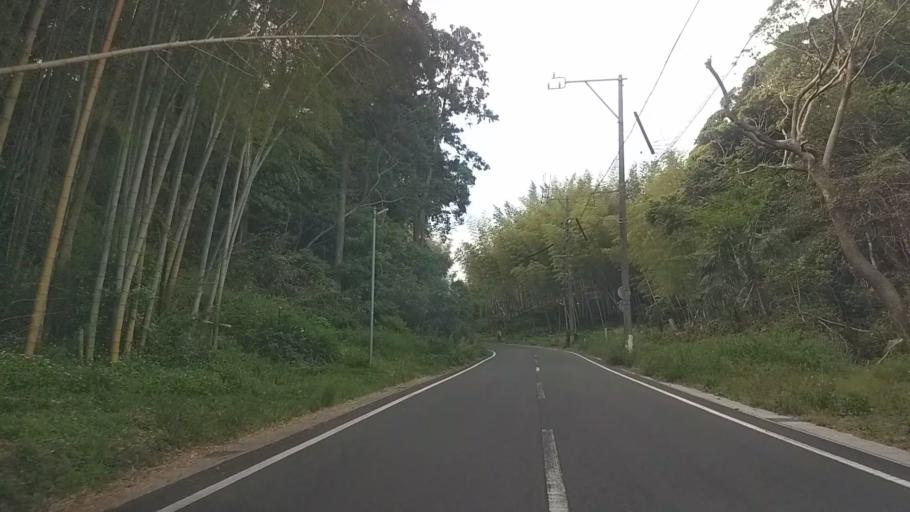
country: JP
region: Shizuoka
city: Hamamatsu
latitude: 34.7189
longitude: 137.6526
